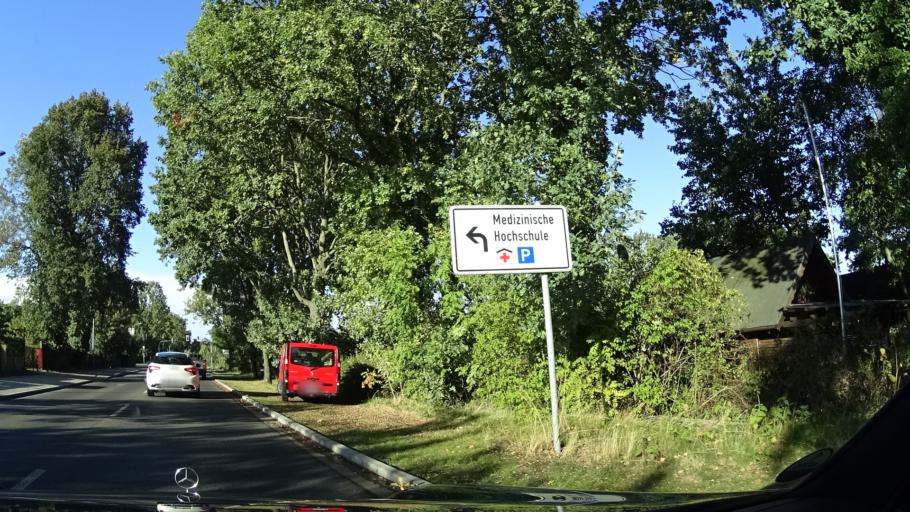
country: DE
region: Brandenburg
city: Neuruppin
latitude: 52.9031
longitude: 12.8005
